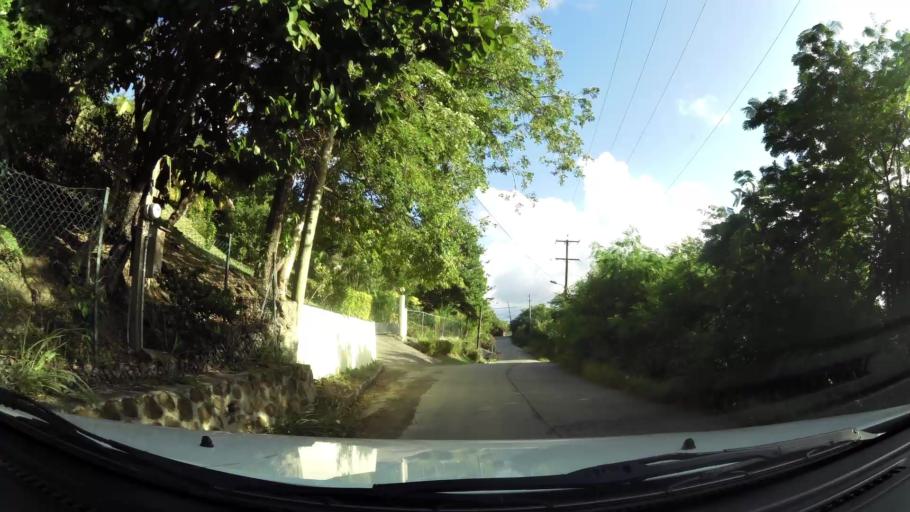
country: LC
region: Gros-Islet
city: Gros Islet
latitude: 14.1049
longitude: -60.9408
